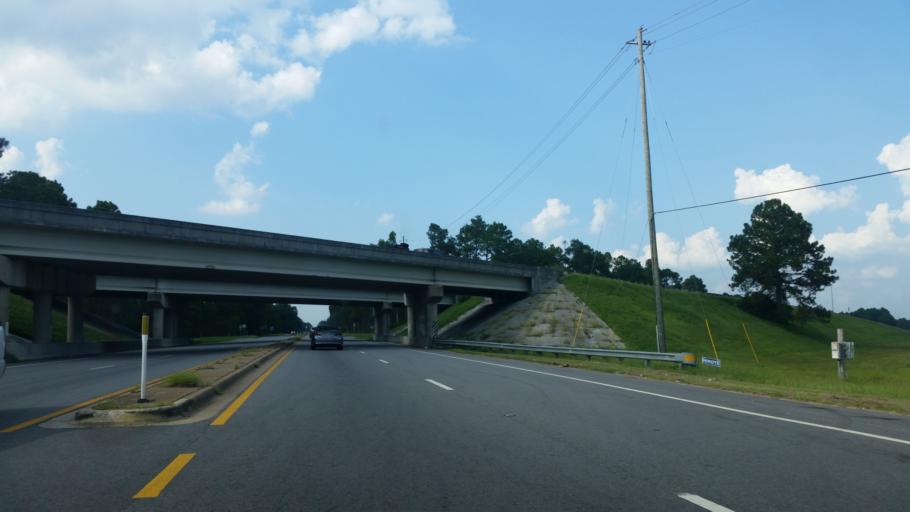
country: US
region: Florida
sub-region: Santa Rosa County
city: Bagdad
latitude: 30.5692
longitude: -87.0315
